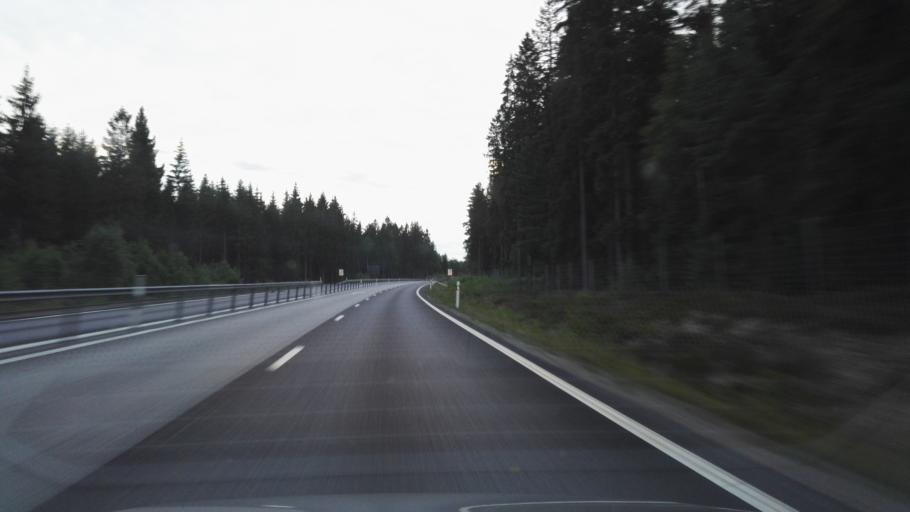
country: SE
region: Kronoberg
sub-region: Vaxjo Kommun
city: Rottne
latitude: 56.9450
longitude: 14.9147
